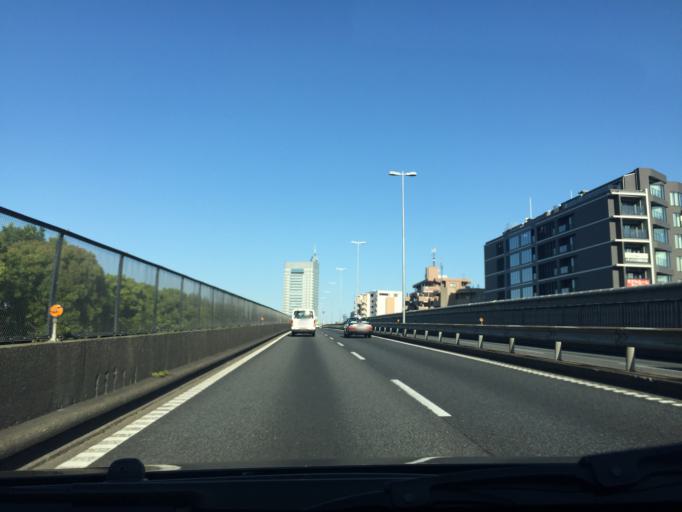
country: JP
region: Tokyo
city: Chofugaoka
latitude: 35.6278
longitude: 139.6231
